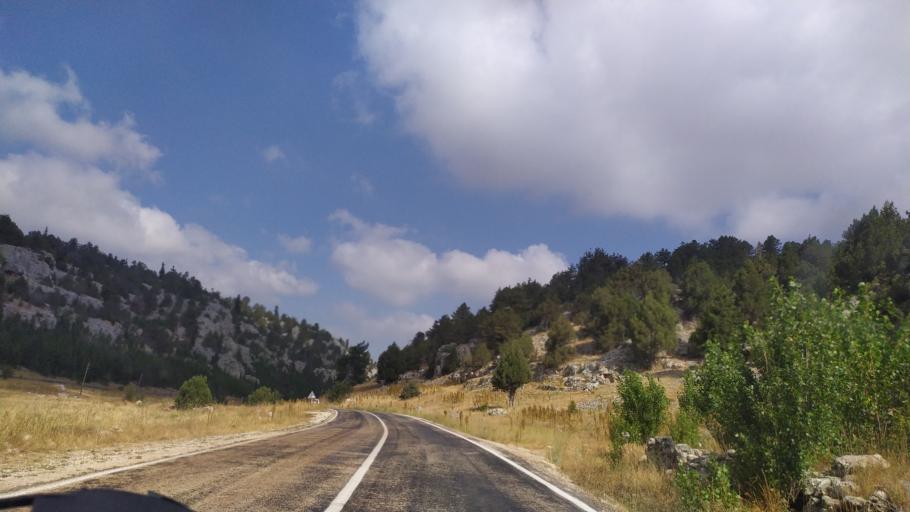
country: TR
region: Mersin
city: Kirobasi
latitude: 36.6148
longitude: 33.8778
